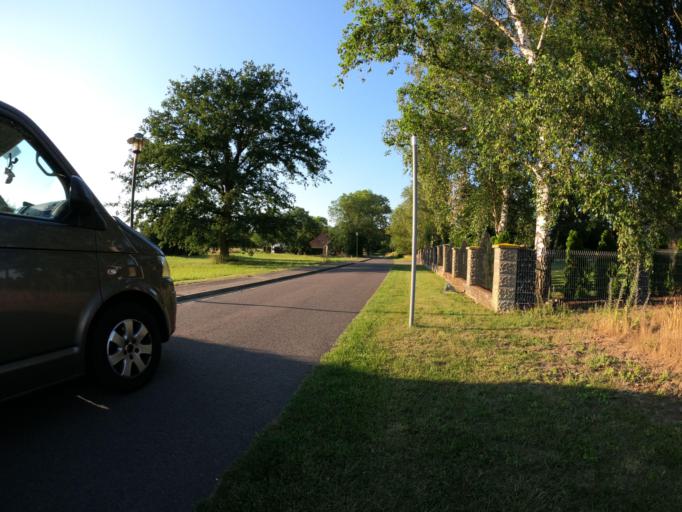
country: DE
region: Brandenburg
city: Tantow
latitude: 53.3019
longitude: 14.3839
